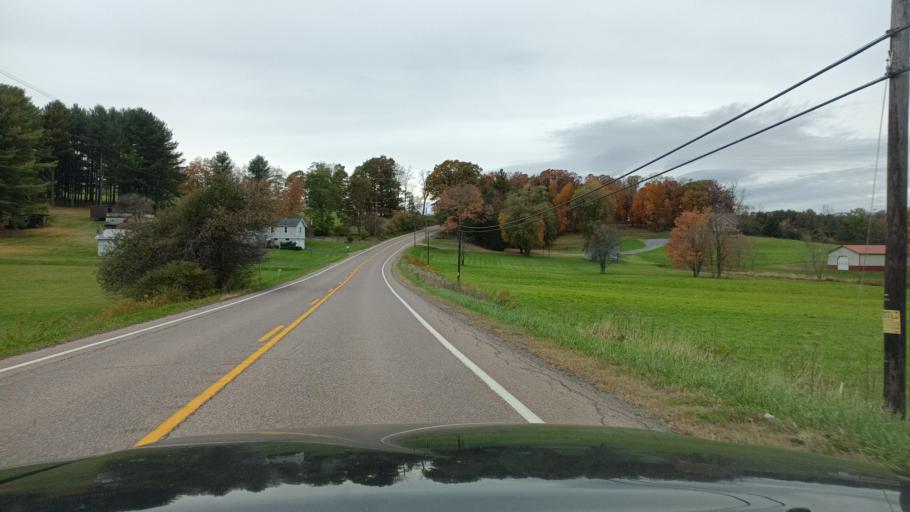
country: US
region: Maryland
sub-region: Garrett County
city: Oakland
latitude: 39.3024
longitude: -79.4464
